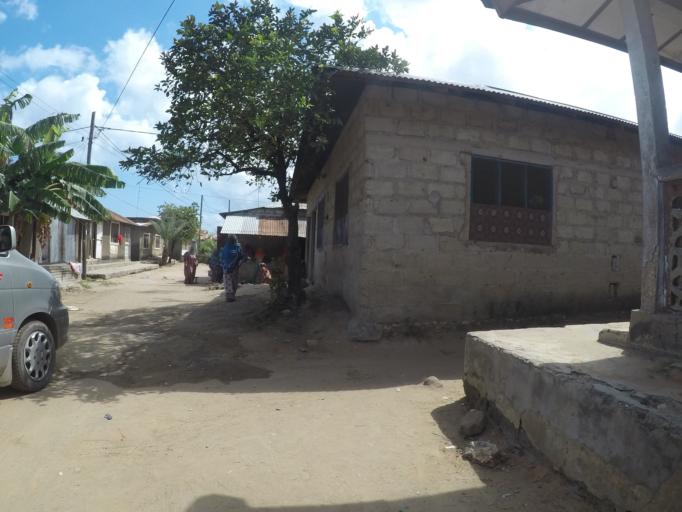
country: TZ
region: Zanzibar Urban/West
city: Zanzibar
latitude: -6.1814
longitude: 39.2122
